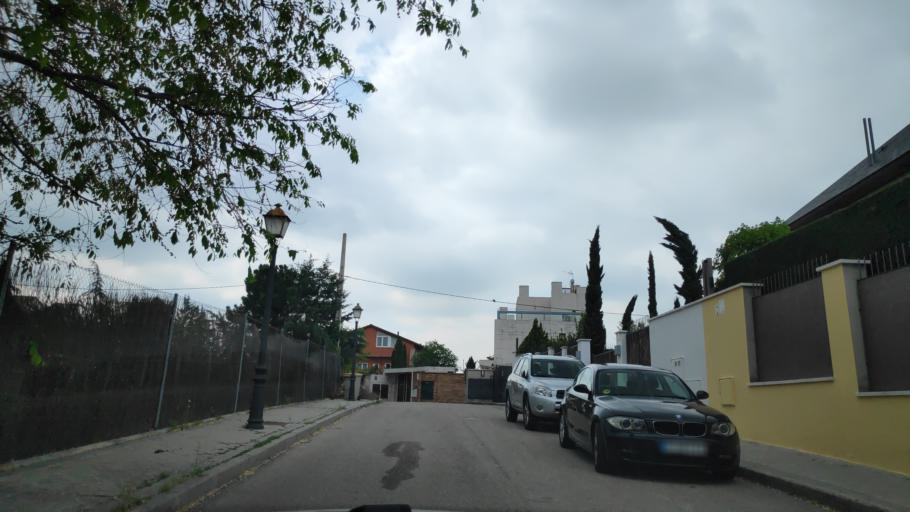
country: ES
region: Madrid
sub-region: Provincia de Madrid
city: Pozuelo de Alarcon
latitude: 40.4634
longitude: -3.7934
